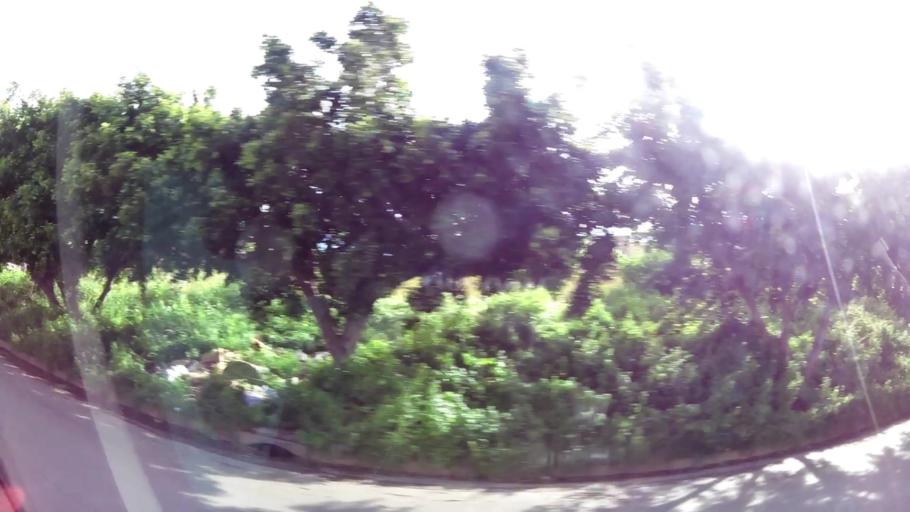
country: MA
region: Grand Casablanca
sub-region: Mohammedia
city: Mohammedia
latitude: 33.6954
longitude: -7.3817
